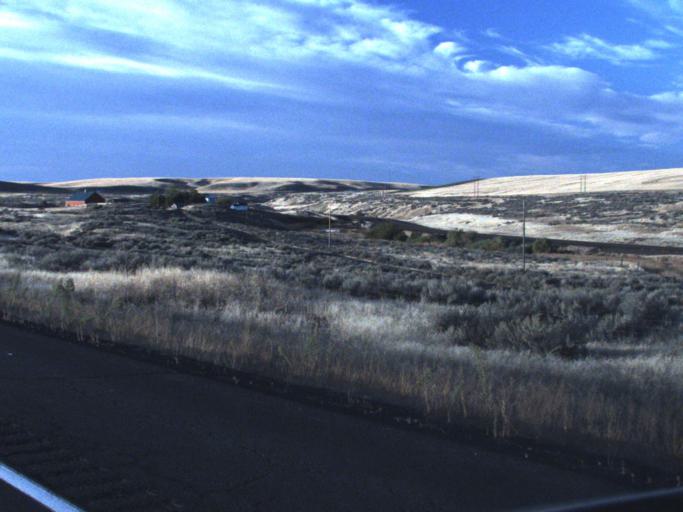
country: US
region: Washington
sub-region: Adams County
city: Ritzville
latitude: 47.0699
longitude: -118.4099
